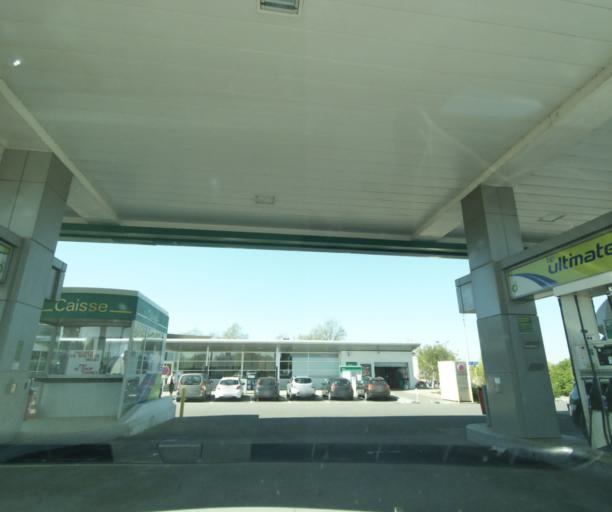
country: FR
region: Centre
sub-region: Departement de l'Indre
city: Vatan
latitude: 47.0903
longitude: 1.8450
